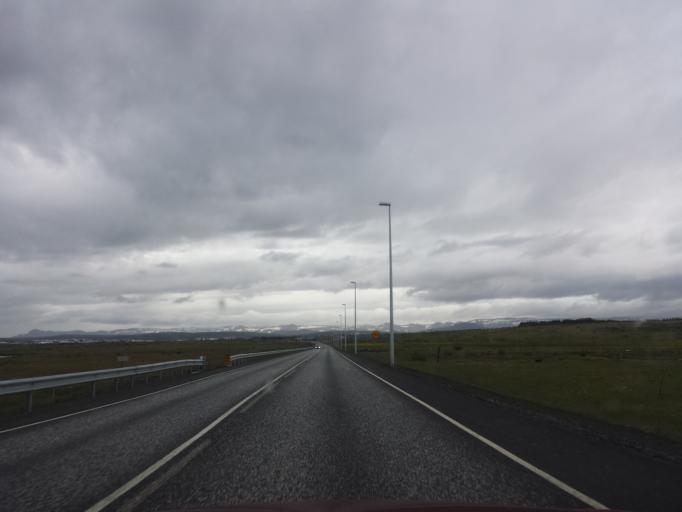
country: IS
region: Capital Region
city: Alftanes
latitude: 64.0965
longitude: -22.0017
